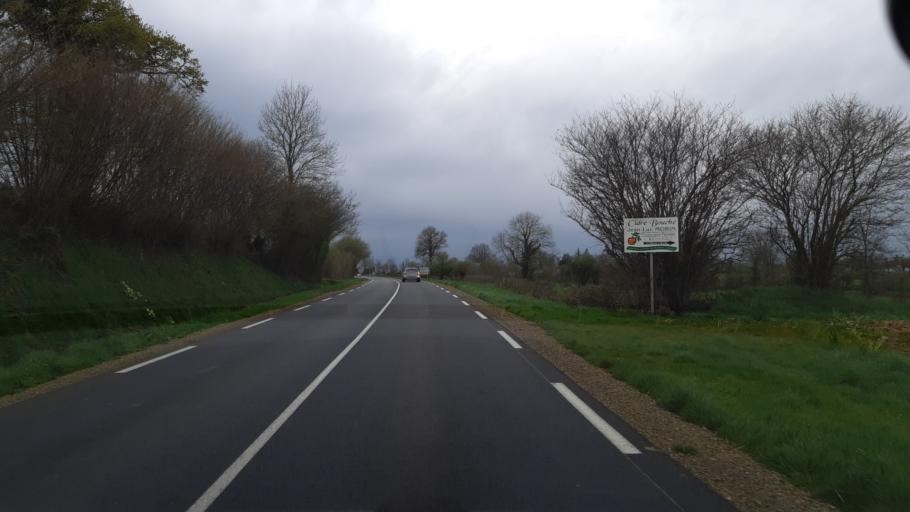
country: FR
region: Lower Normandy
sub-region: Departement de la Manche
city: Percy
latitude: 48.9578
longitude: -1.1962
